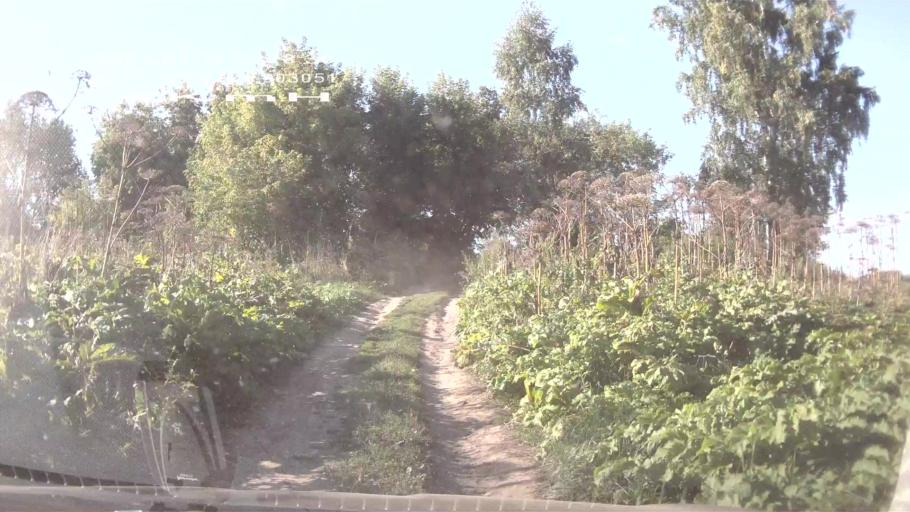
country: RU
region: Mariy-El
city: Morki
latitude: 56.3594
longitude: 48.9029
